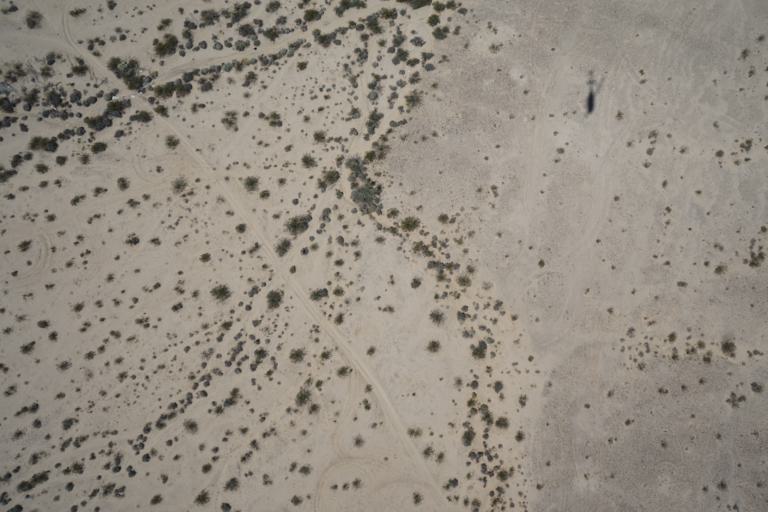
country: US
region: California
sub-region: San Bernardino County
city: Twentynine Palms
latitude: 34.1334
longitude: -116.0311
